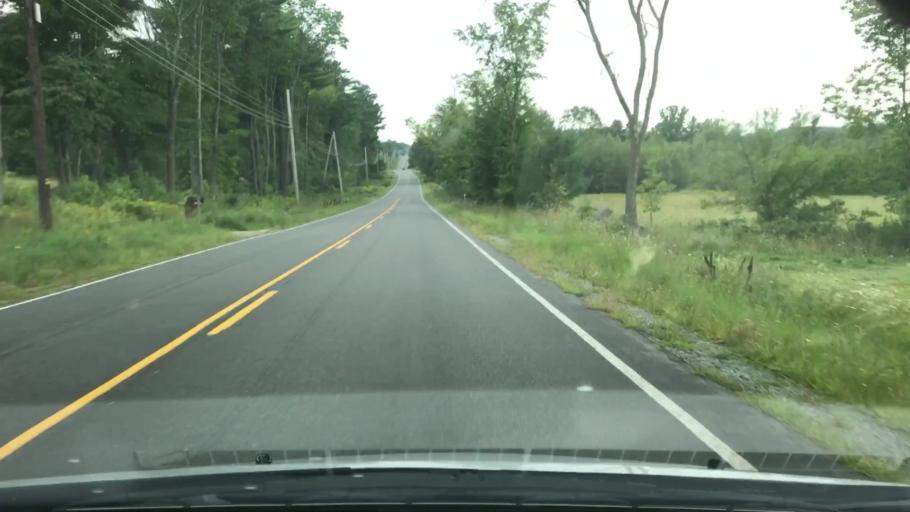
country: US
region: New Hampshire
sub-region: Grafton County
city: Haverhill
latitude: 44.0143
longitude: -72.0683
